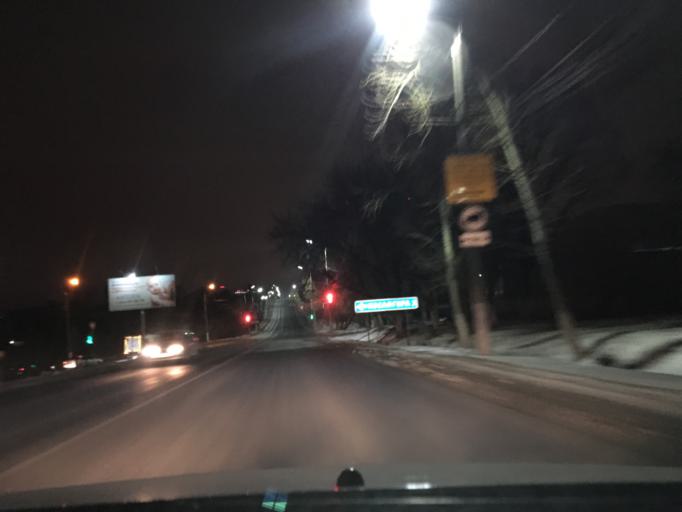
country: RU
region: Tula
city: Mendeleyevskiy
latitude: 54.1340
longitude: 37.5792
